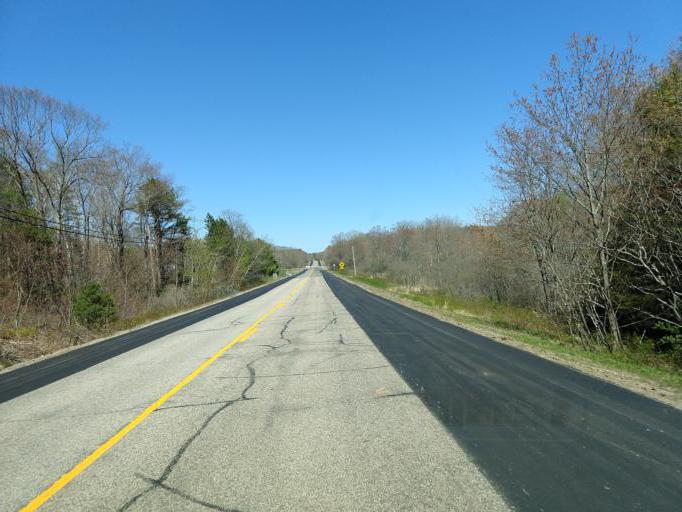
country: US
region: Maine
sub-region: York County
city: Arundel
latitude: 43.4030
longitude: -70.4303
